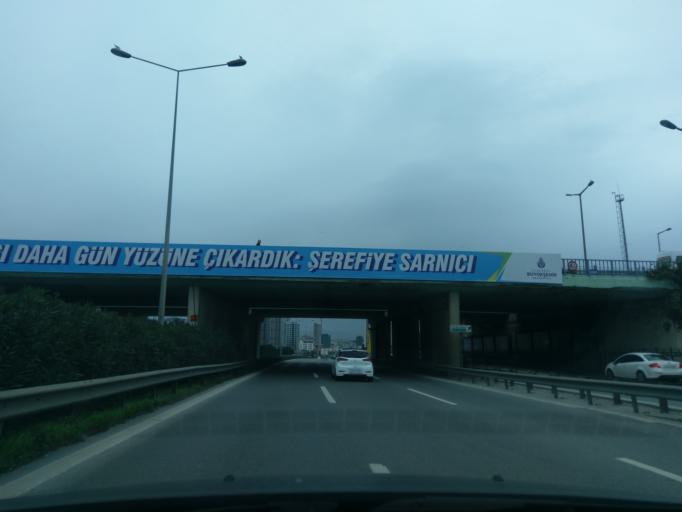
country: TR
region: Istanbul
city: Maltepe
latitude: 40.9064
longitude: 29.2103
